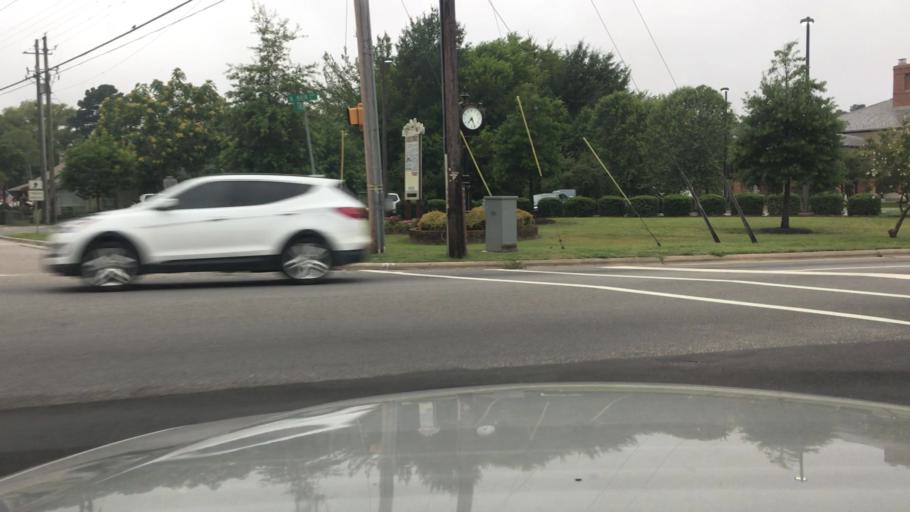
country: US
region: North Carolina
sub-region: Cumberland County
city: Hope Mills
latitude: 34.9723
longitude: -78.9460
